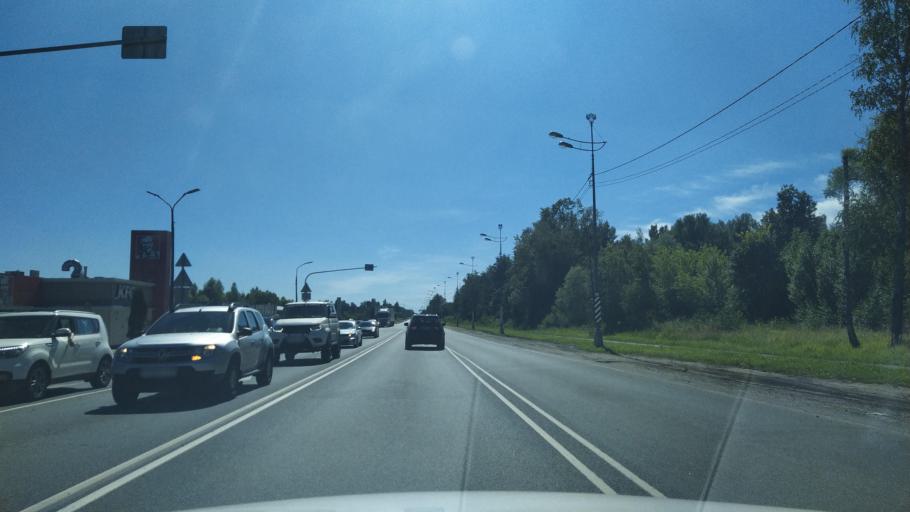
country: RU
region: Pskov
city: Pskov
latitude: 57.7945
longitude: 28.4164
